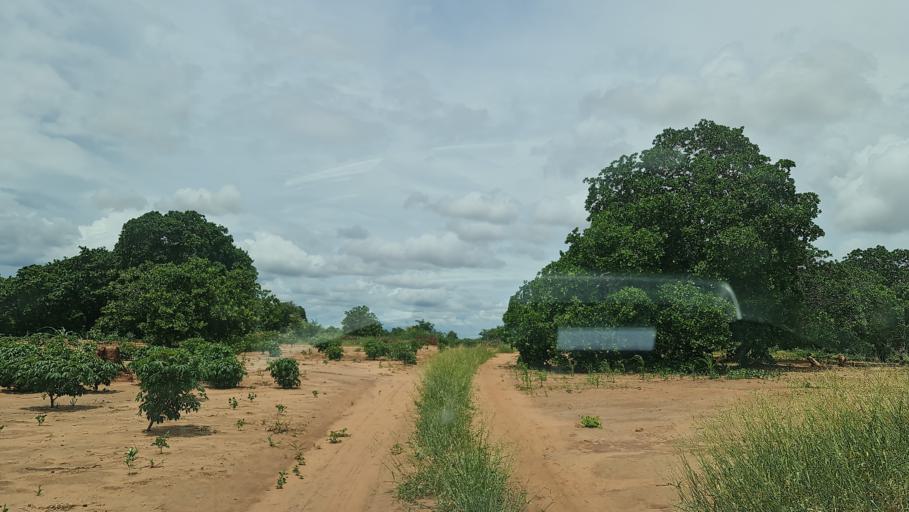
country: MZ
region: Nampula
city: Nacala
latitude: -14.7906
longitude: 39.9676
